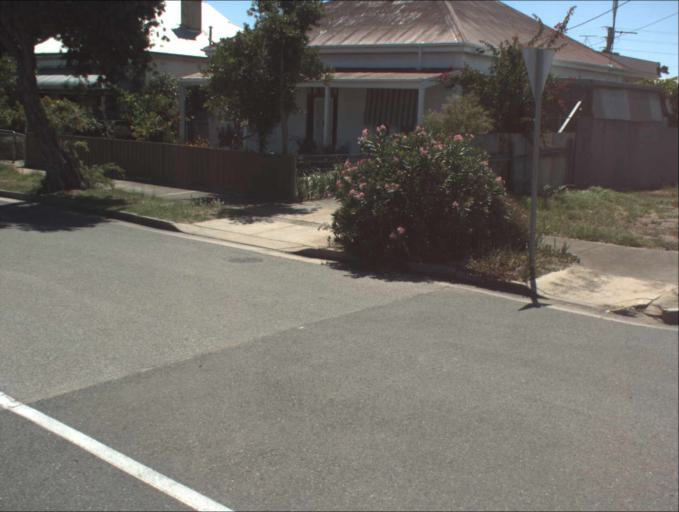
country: AU
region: South Australia
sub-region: Port Adelaide Enfield
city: Cheltenham
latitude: -34.8639
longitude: 138.5133
